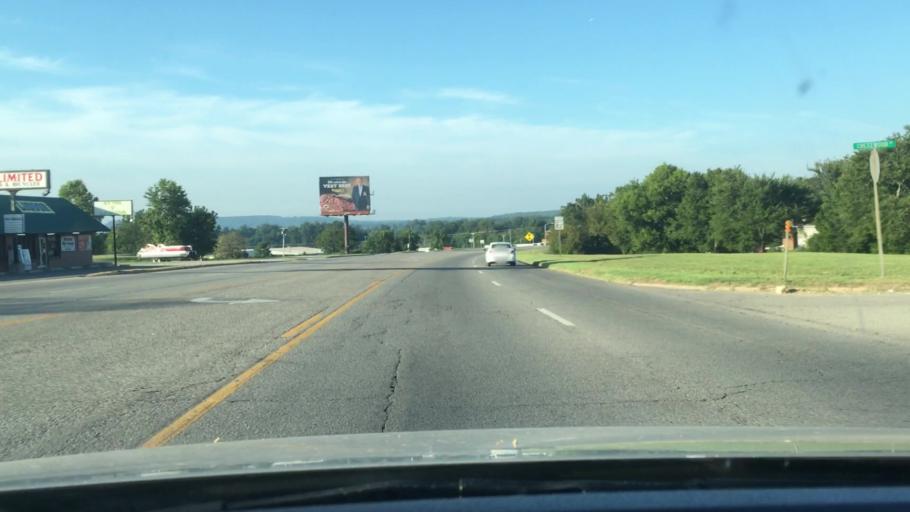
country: US
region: Oklahoma
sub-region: Cherokee County
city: Park Hill
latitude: 35.8612
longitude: -94.9773
